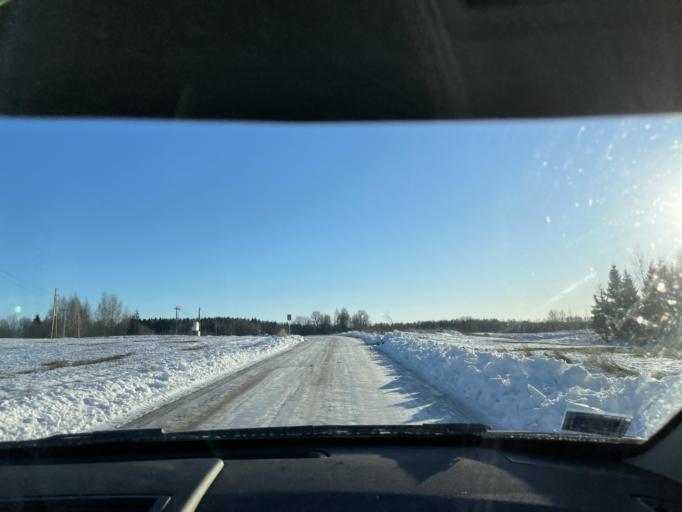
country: LV
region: Ludzas Rajons
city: Ludza
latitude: 56.4599
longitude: 27.6352
